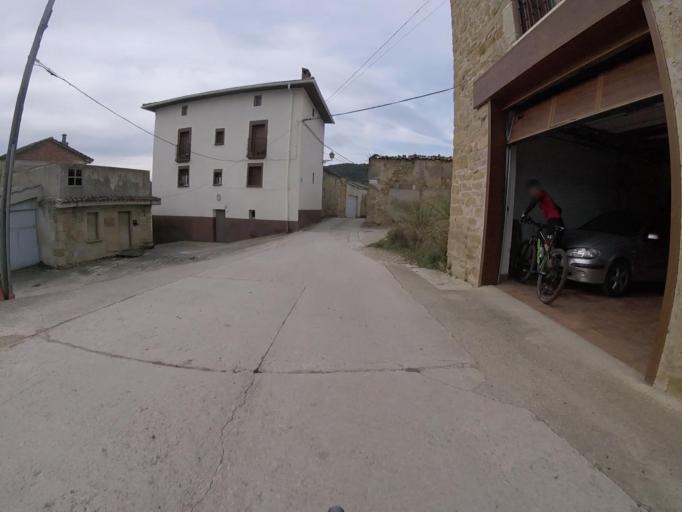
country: ES
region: Navarre
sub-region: Provincia de Navarra
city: Estella
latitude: 42.7164
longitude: -2.0487
